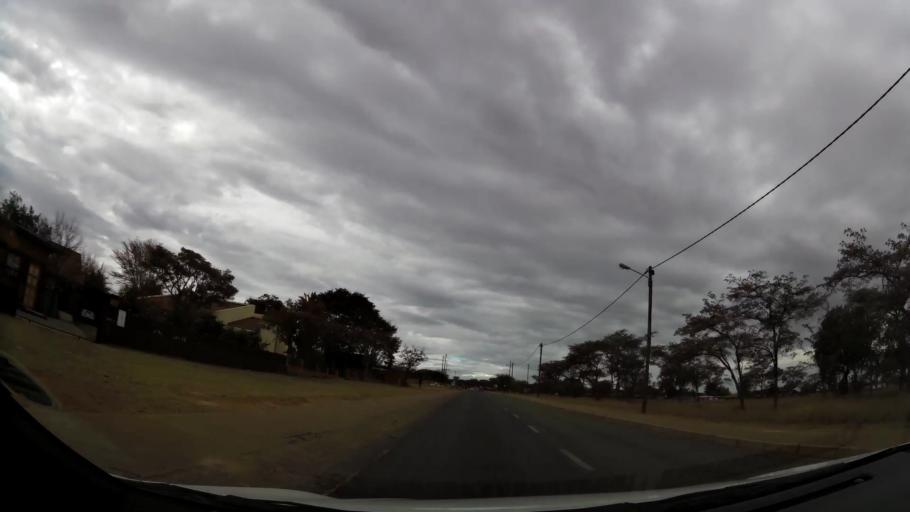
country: ZA
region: Limpopo
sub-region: Waterberg District Municipality
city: Modimolle
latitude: -24.6985
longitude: 28.4184
